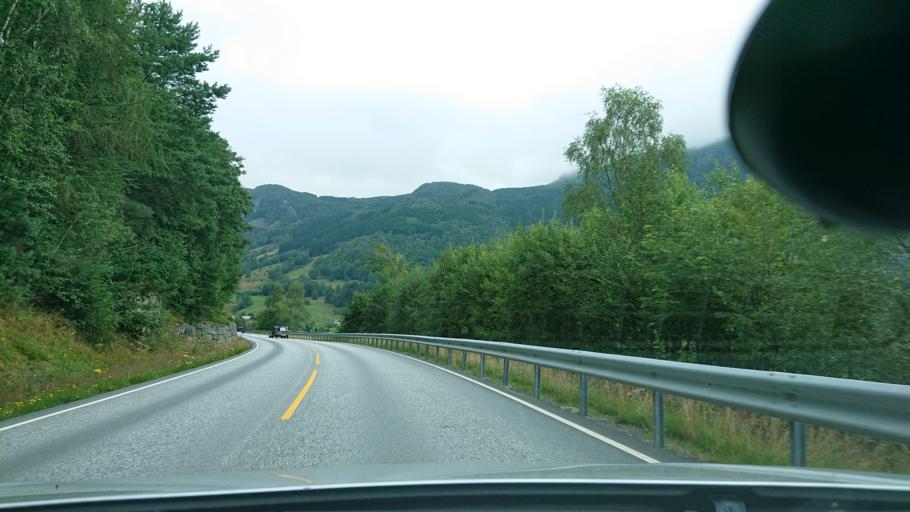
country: NO
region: Rogaland
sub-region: Hjelmeland
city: Hjelmelandsvagen
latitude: 59.1591
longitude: 6.1747
